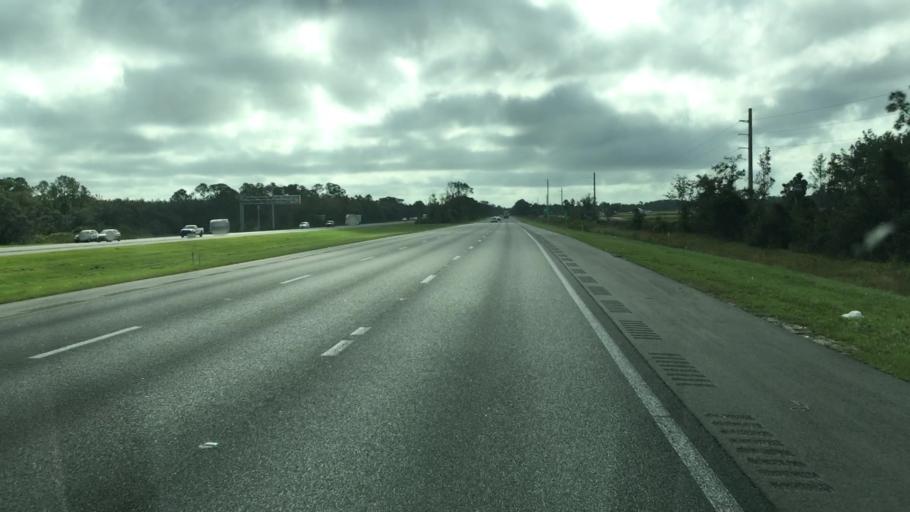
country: US
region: Florida
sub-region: Volusia County
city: Samsula-Spruce Creek
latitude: 29.0844
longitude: -81.0183
